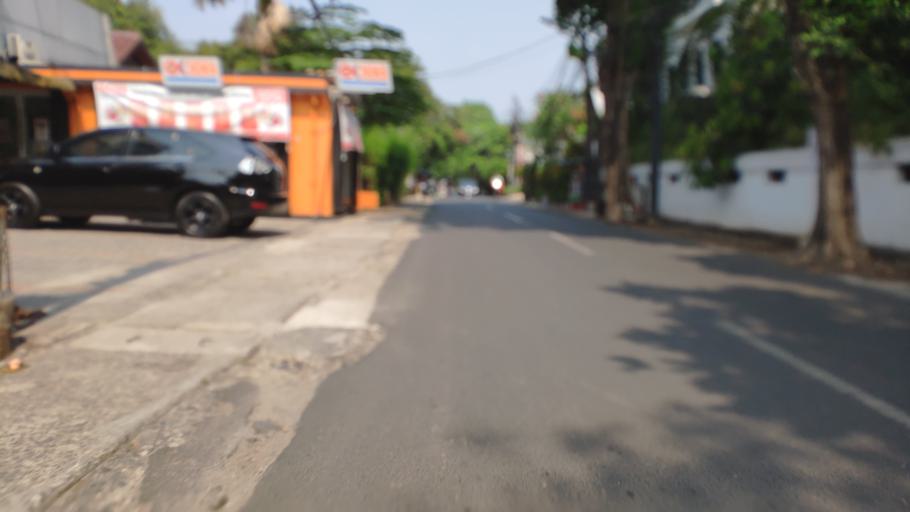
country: ID
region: Jakarta Raya
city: Jakarta
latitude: -6.2546
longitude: 106.8152
